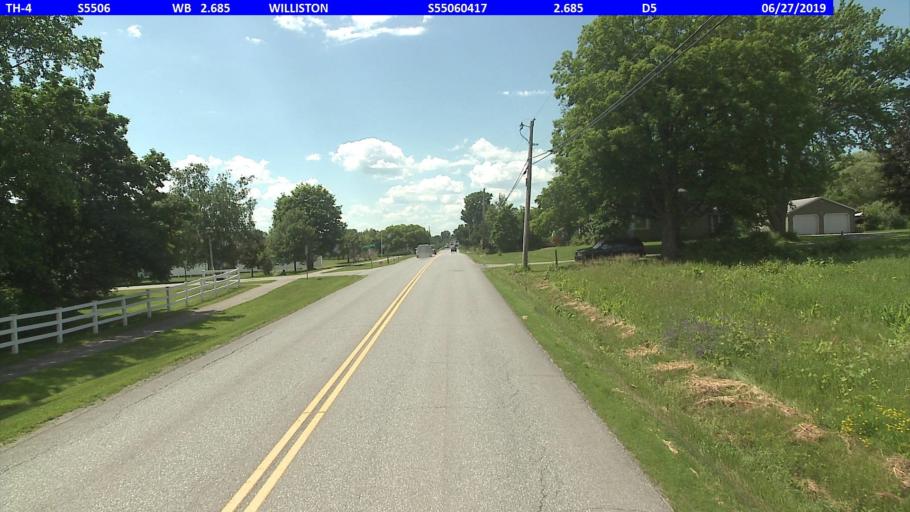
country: US
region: Vermont
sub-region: Chittenden County
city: Williston
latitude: 44.4520
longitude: -73.0647
